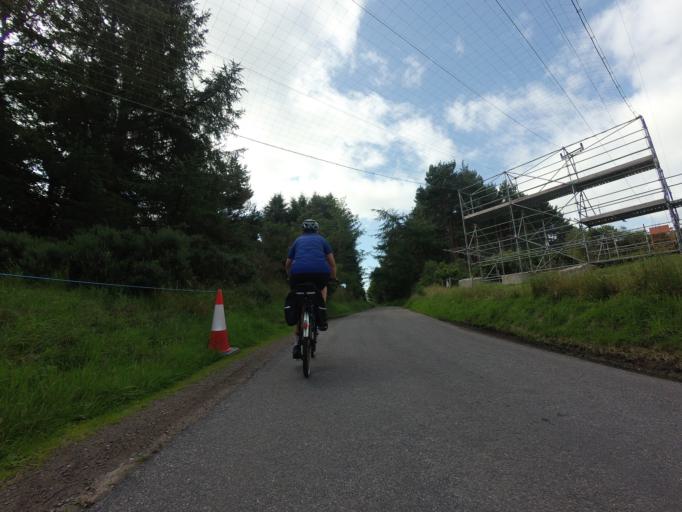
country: GB
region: Scotland
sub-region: Highland
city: Nairn
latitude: 57.5680
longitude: -3.8660
